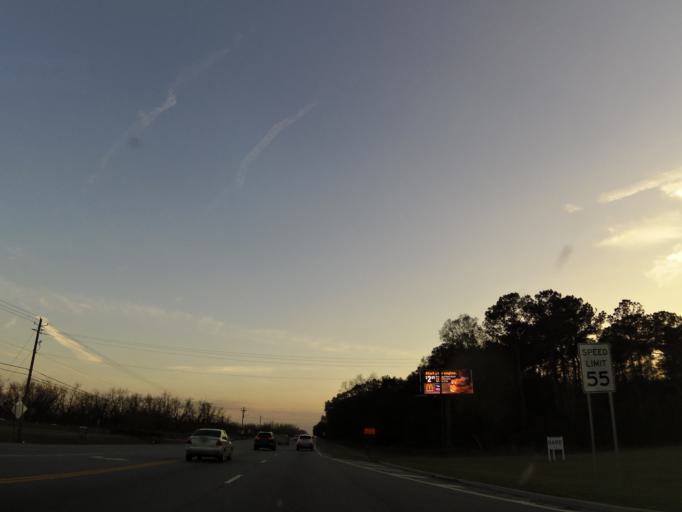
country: US
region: Georgia
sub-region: Lee County
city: Leesburg
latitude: 31.6557
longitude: -84.1732
